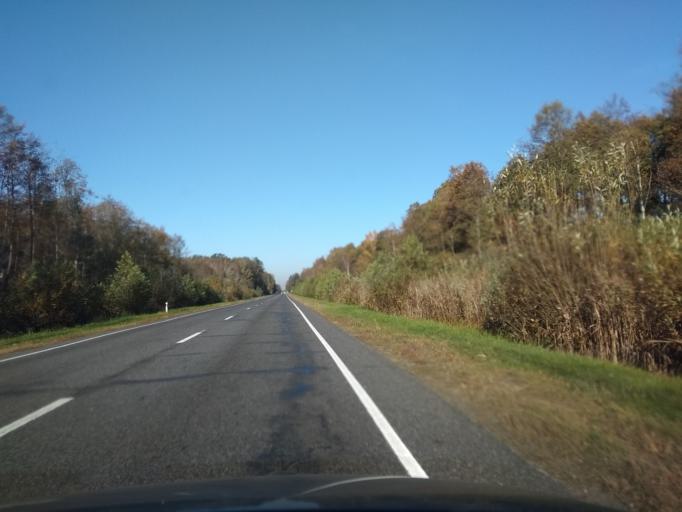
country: BY
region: Brest
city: Malaryta
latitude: 51.9176
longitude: 24.0887
